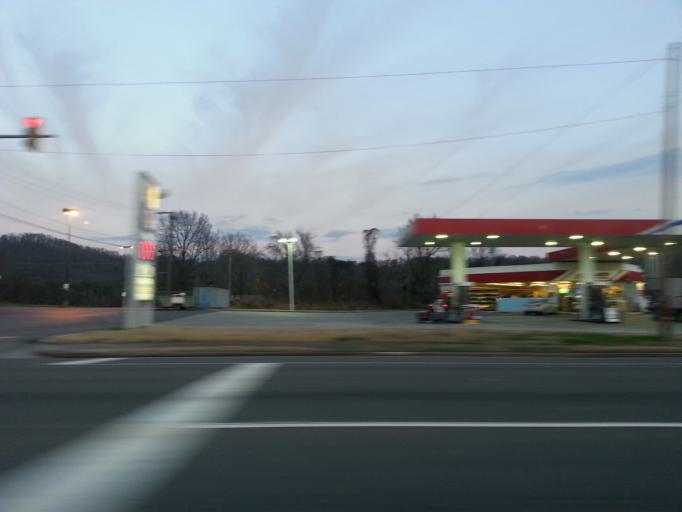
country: US
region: Tennessee
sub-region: McMinn County
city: Etowah
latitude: 35.3409
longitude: -84.5204
